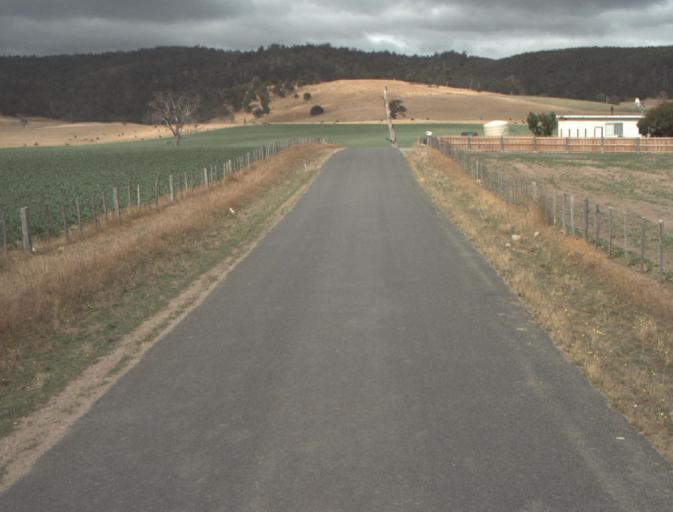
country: AU
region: Tasmania
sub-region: Dorset
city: Scottsdale
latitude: -41.4714
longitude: 147.5888
